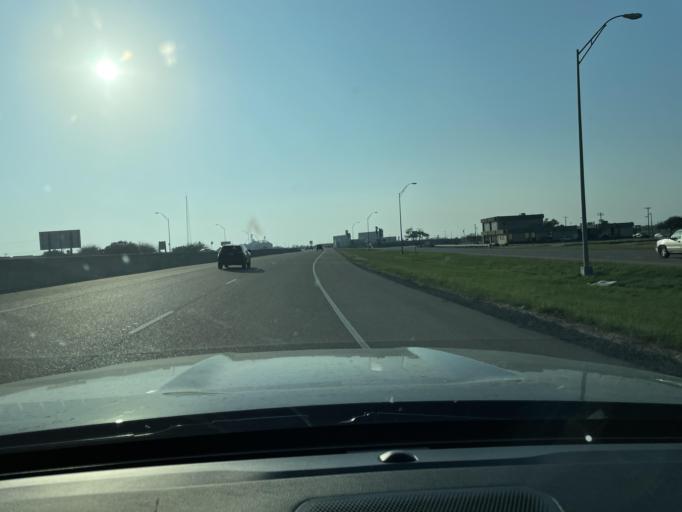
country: US
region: Texas
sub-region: Nueces County
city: Robstown
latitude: 27.7806
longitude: -97.6587
